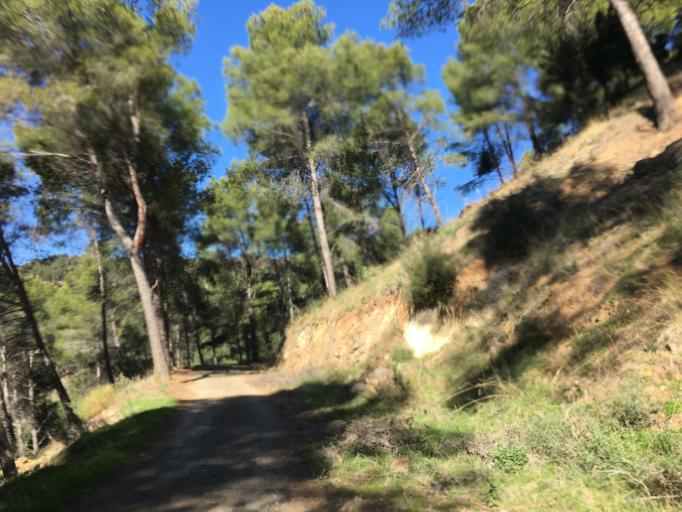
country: ES
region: Andalusia
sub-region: Provincia de Malaga
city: Malaga
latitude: 36.8001
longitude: -4.3992
